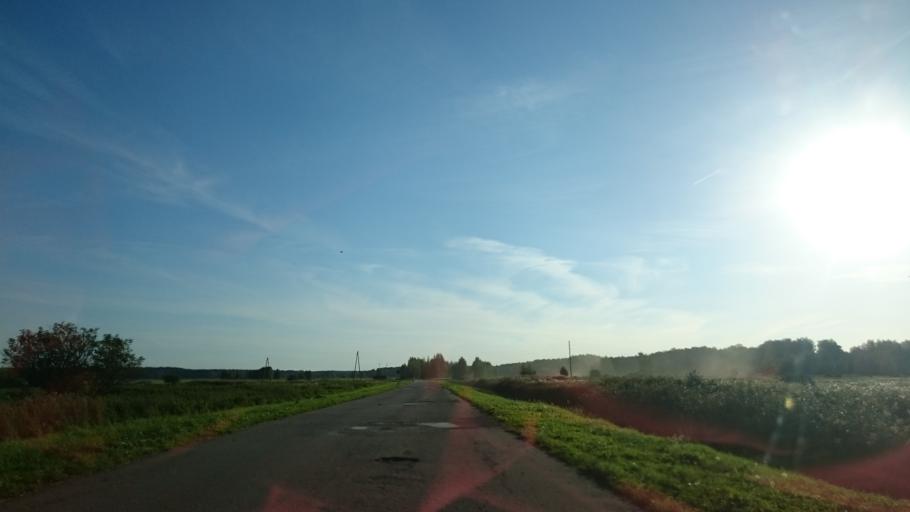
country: LV
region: Riga
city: Jaunciems
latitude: 57.0972
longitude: 24.1996
